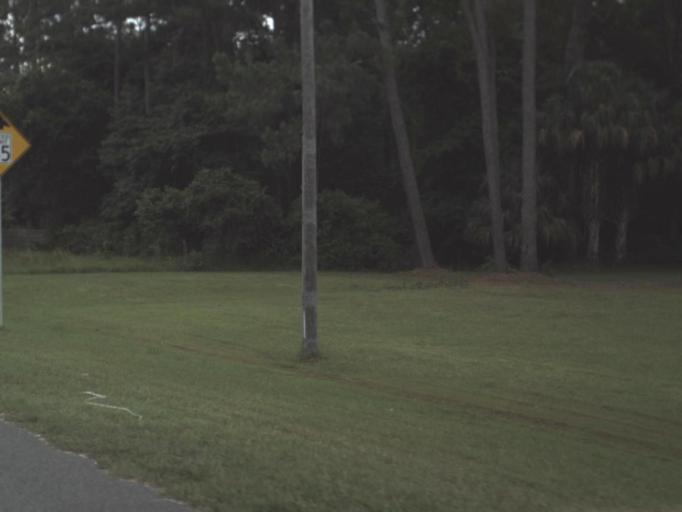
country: US
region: Florida
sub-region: Putnam County
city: East Palatka
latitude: 29.5967
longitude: -81.5968
